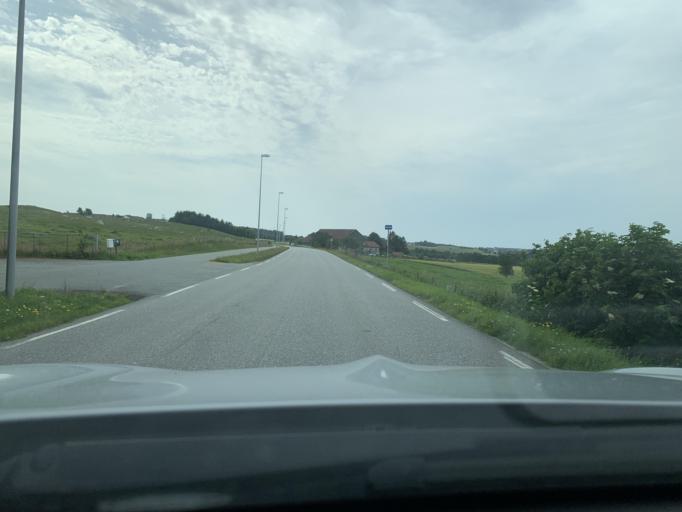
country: NO
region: Rogaland
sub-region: Time
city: Bryne
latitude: 58.7484
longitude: 5.6927
